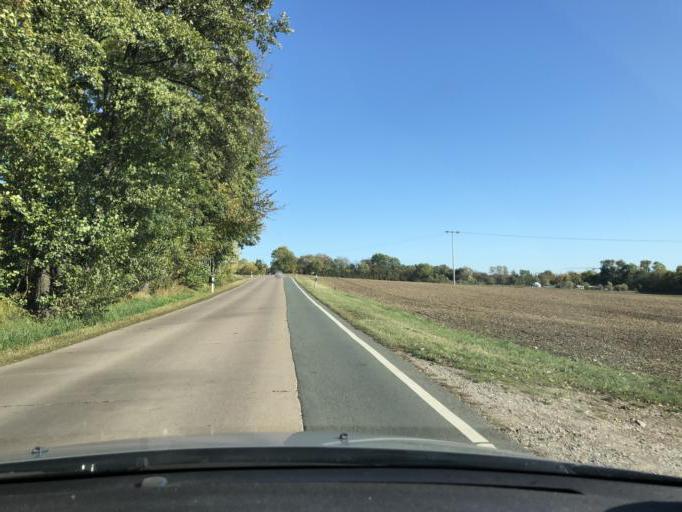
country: DE
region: Thuringia
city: Hopfgarten
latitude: 50.9941
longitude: 11.2966
